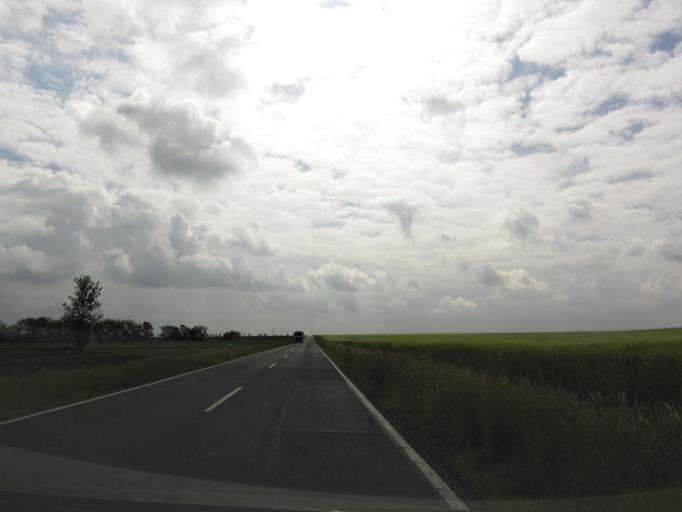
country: DE
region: Thuringia
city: Apfelstadt
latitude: 50.9247
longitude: 10.8790
